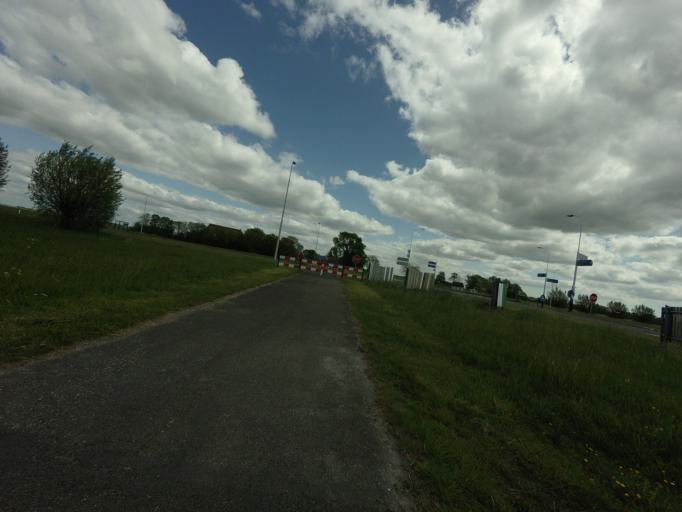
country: NL
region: Friesland
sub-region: Sudwest Fryslan
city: Bolsward
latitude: 53.0937
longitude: 5.5340
